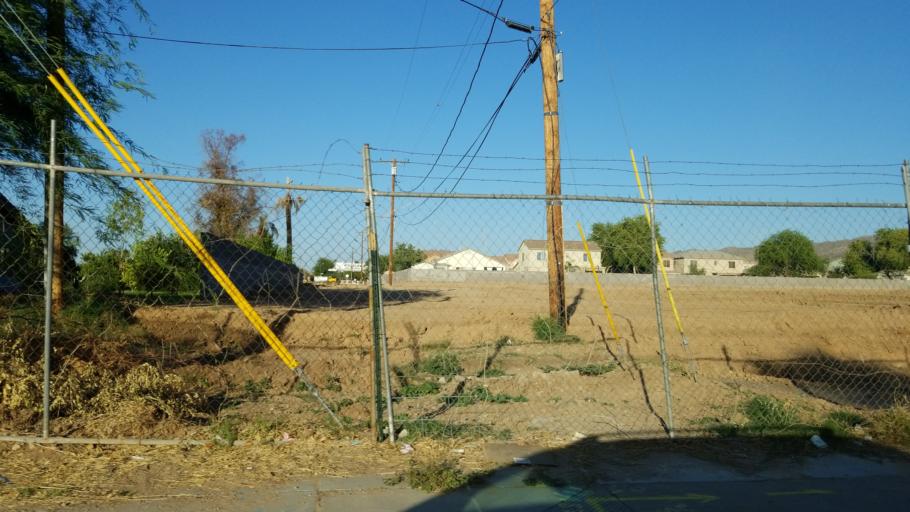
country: US
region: Arizona
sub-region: Maricopa County
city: Phoenix
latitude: 33.3739
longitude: -112.0833
